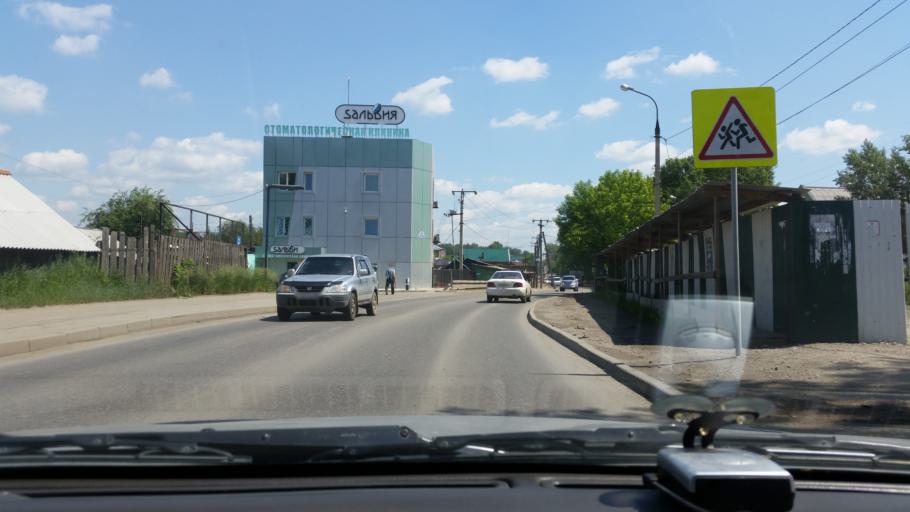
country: RU
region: Irkutsk
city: Dzerzhinsk
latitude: 52.2790
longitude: 104.3619
